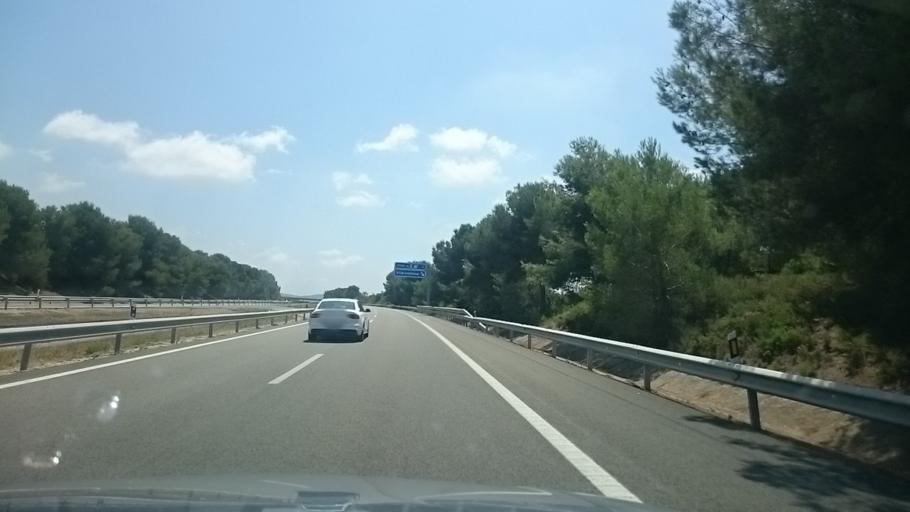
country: ES
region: Catalonia
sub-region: Provincia de Tarragona
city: Alio
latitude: 41.3114
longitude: 1.3373
